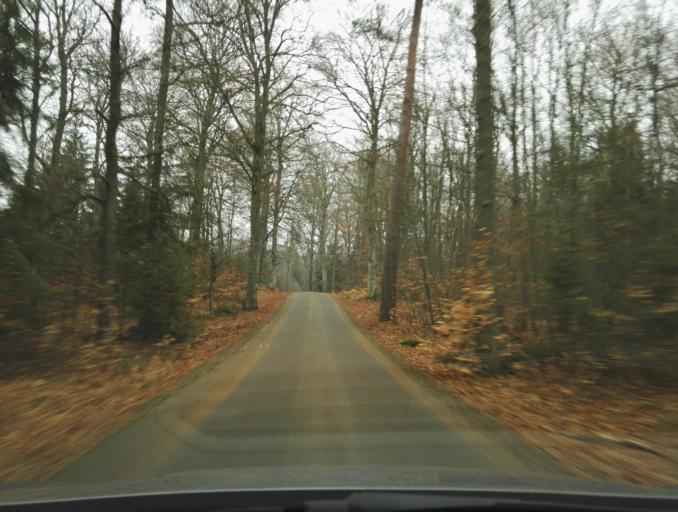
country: SE
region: Kronoberg
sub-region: Vaxjo Kommun
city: Vaexjoe
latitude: 56.9518
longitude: 14.7983
